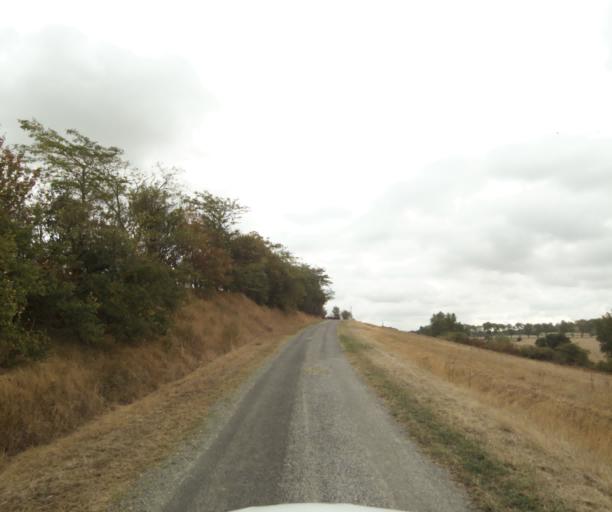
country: FR
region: Midi-Pyrenees
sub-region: Departement de la Haute-Garonne
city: Villefranche-de-Lauragais
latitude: 43.4179
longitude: 1.7340
